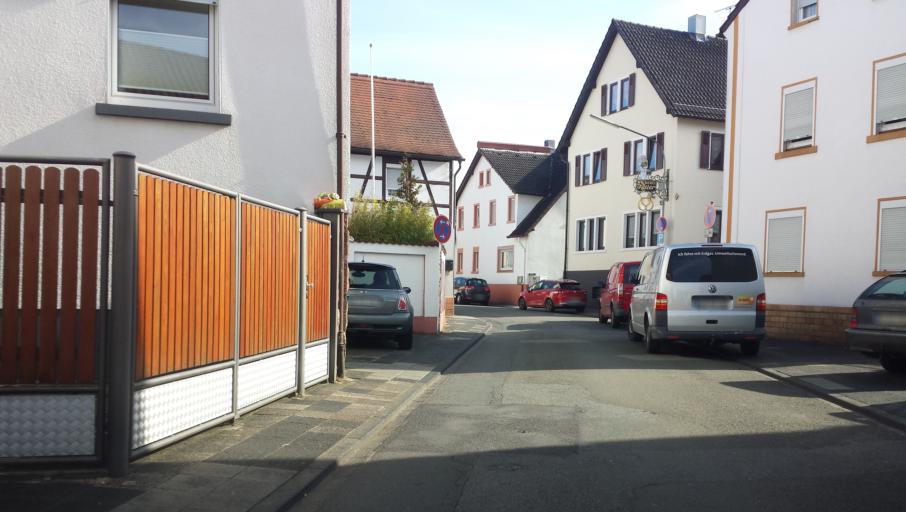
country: DE
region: Hesse
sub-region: Regierungsbezirk Darmstadt
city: Erzhausen
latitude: 49.9531
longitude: 8.6339
